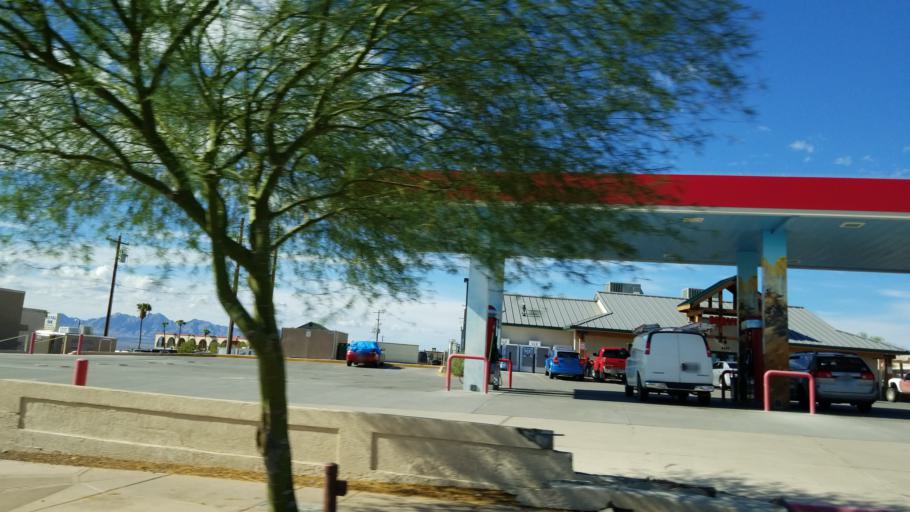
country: US
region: Arizona
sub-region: Mohave County
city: Lake Havasu City
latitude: 34.4755
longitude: -114.3229
